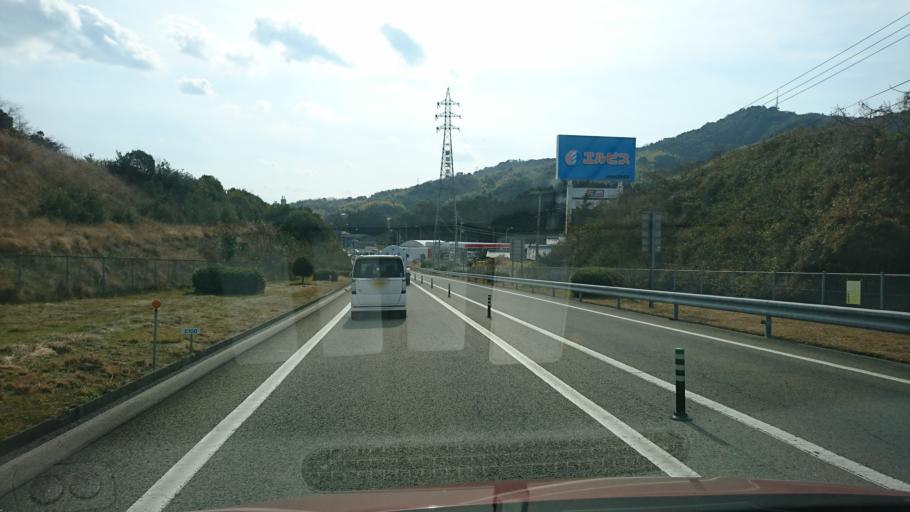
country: JP
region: Ehime
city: Hojo
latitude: 34.0952
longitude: 132.9773
